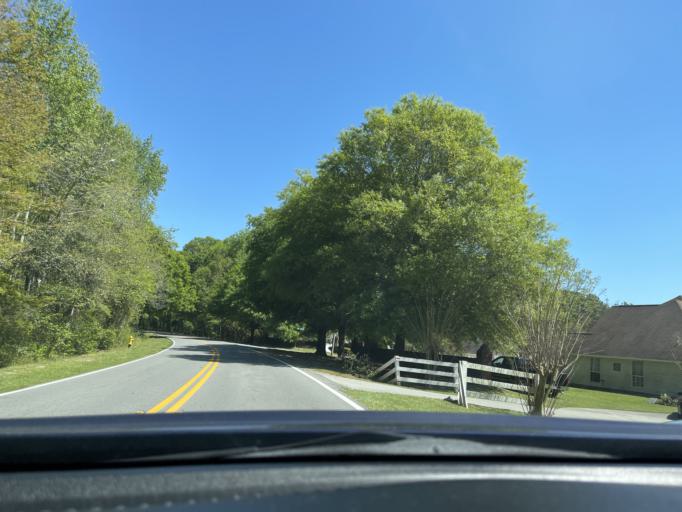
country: US
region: Georgia
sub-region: Chatham County
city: Pooler
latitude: 32.0900
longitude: -81.2474
